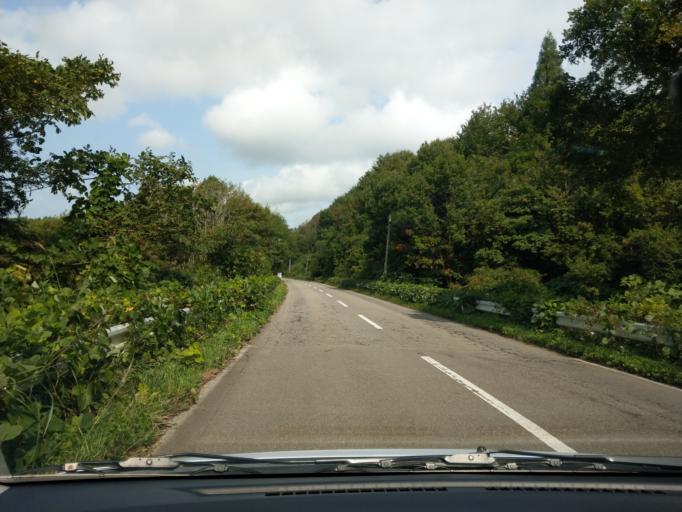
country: JP
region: Akita
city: Omagari
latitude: 39.4880
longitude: 140.3136
